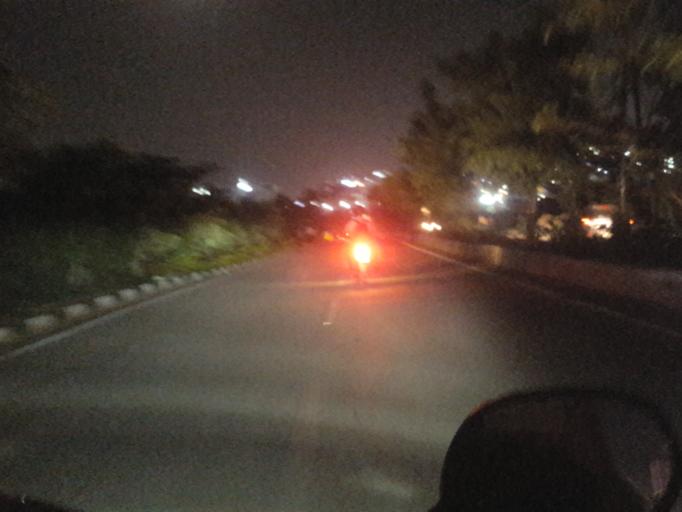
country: IN
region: Telangana
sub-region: Rangareddi
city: Kukatpalli
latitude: 17.4421
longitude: 78.3719
